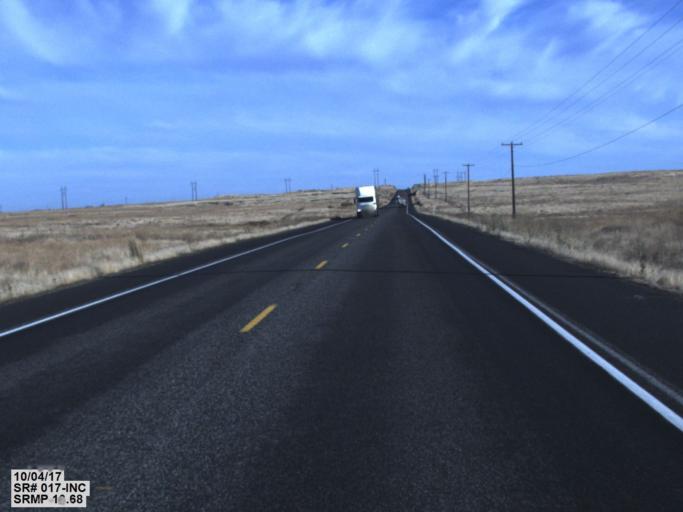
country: US
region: Washington
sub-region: Franklin County
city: Connell
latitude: 46.6504
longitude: -119.0064
